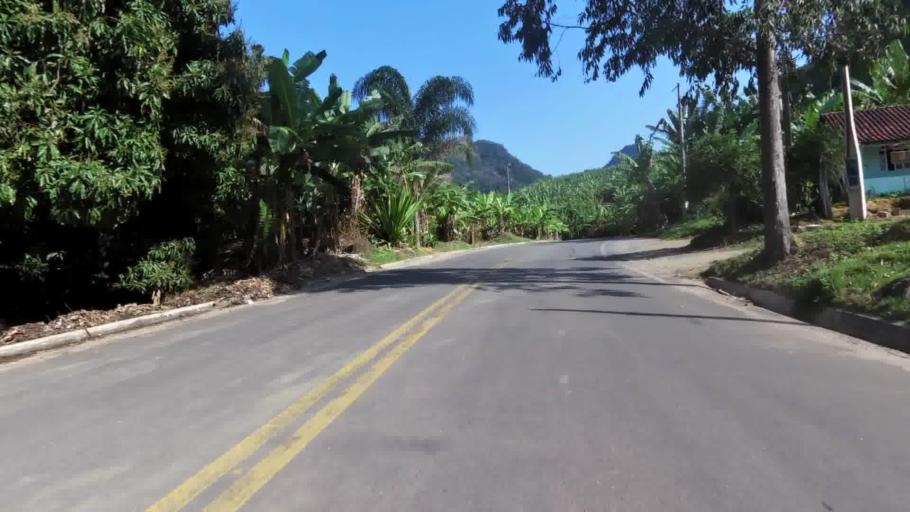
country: BR
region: Espirito Santo
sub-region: Alfredo Chaves
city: Alfredo Chaves
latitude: -20.6256
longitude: -40.7720
